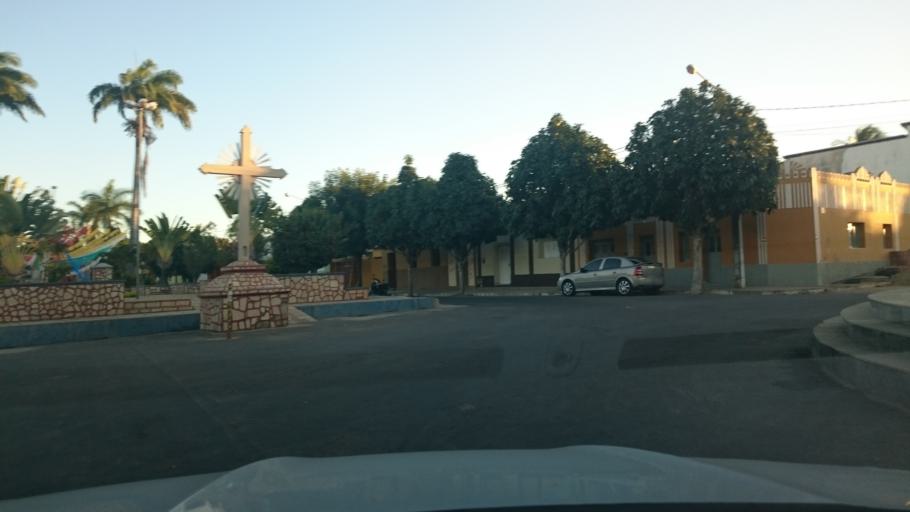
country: BR
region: Rio Grande do Norte
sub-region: Umarizal
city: Umarizal
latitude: -6.0236
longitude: -37.9872
